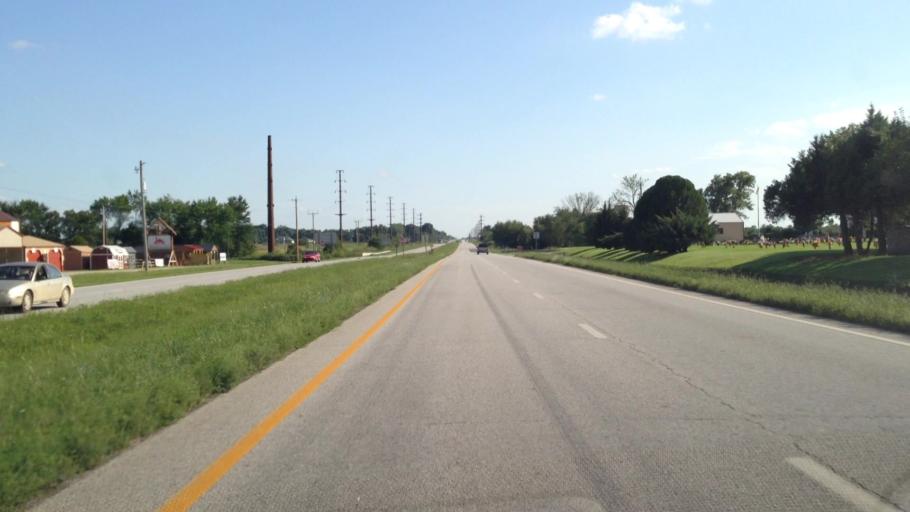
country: US
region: Kansas
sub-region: Crawford County
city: Arma
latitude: 37.5078
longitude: -94.7053
